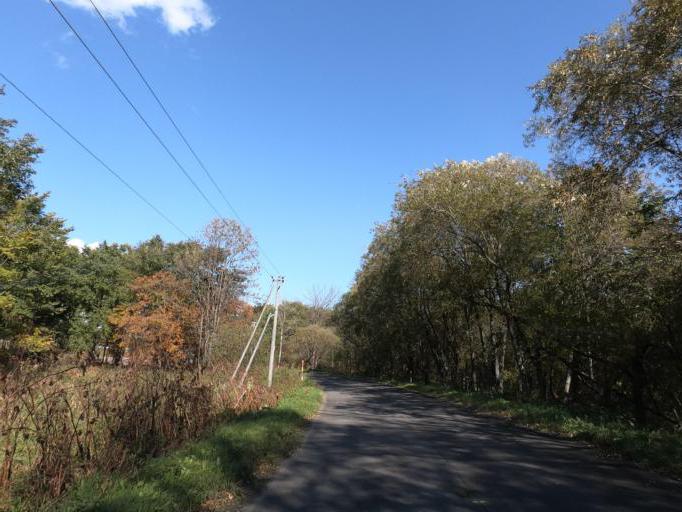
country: JP
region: Hokkaido
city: Otofuke
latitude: 43.2363
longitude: 143.2678
